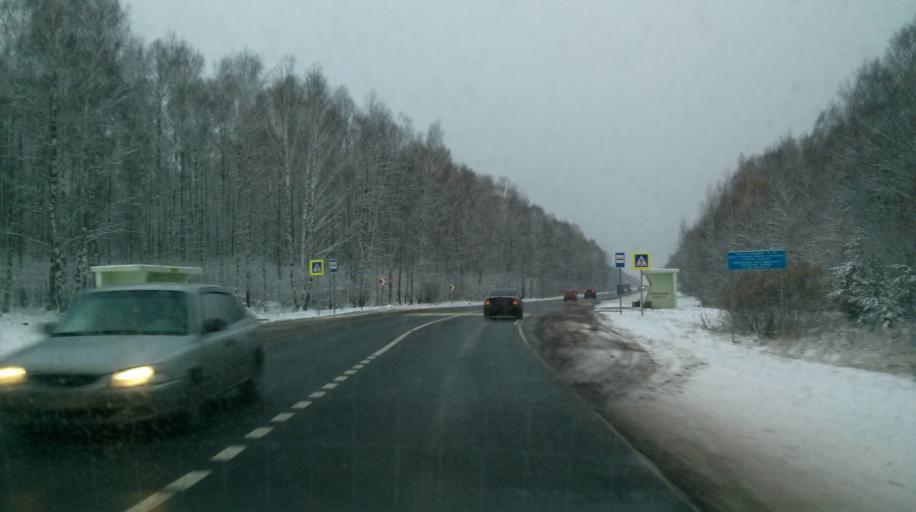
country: RU
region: Nizjnij Novgorod
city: Vorsma
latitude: 56.0131
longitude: 43.3433
